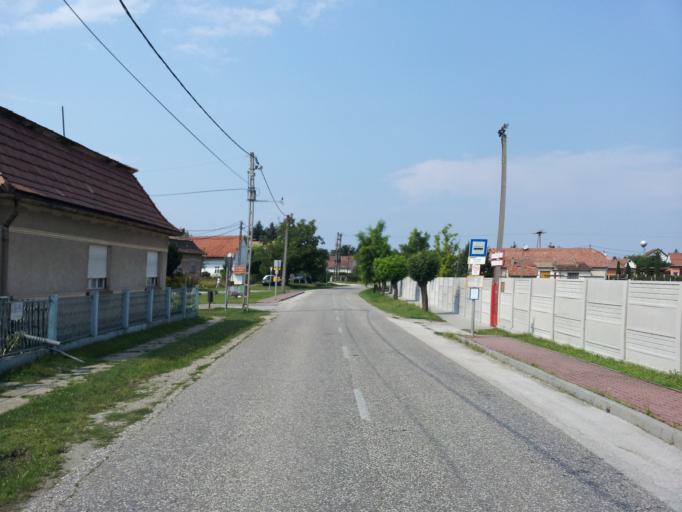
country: HU
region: Pest
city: Szigetujfalu
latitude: 47.2299
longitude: 18.9209
